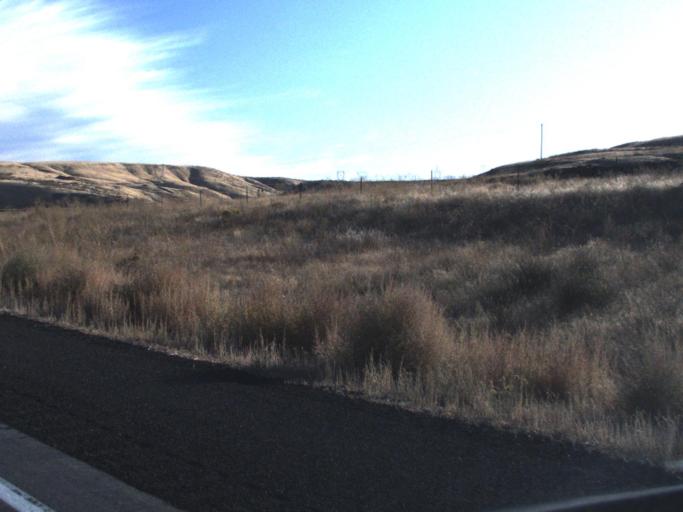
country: US
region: Washington
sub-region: Franklin County
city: Basin City
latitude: 46.5402
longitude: -119.0109
